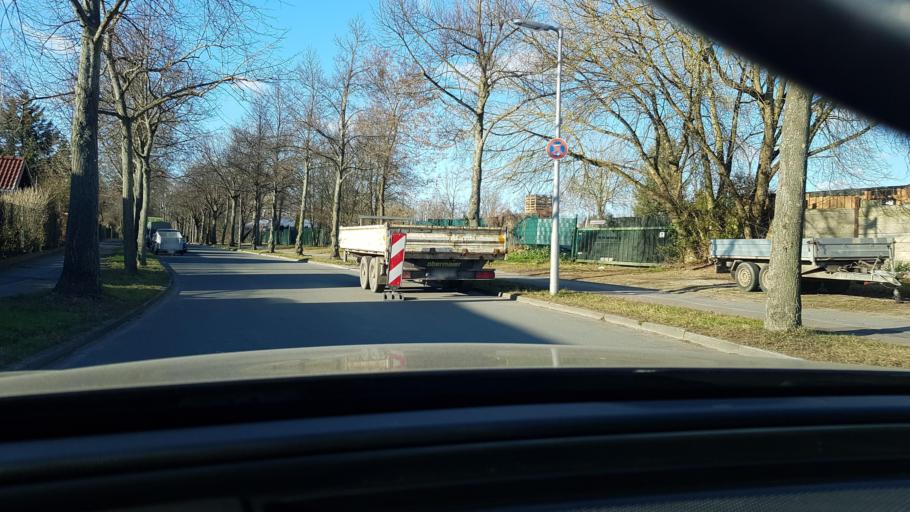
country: DE
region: Berlin
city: Rudow
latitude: 52.4117
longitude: 13.4908
